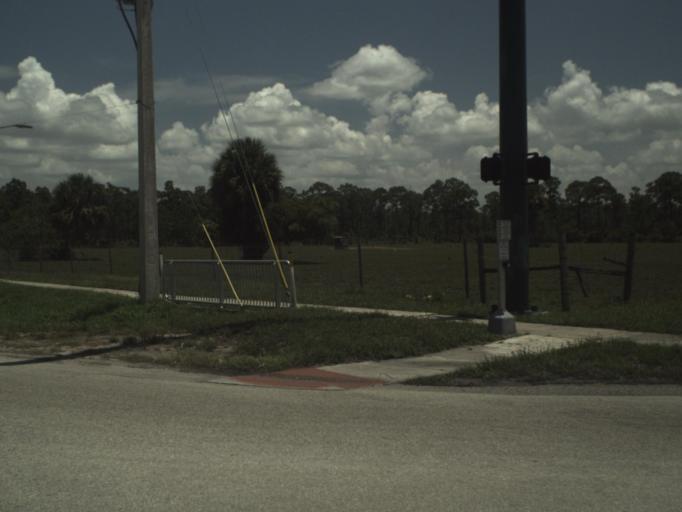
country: US
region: Florida
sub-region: Martin County
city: Palm City
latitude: 27.1616
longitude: -80.3188
